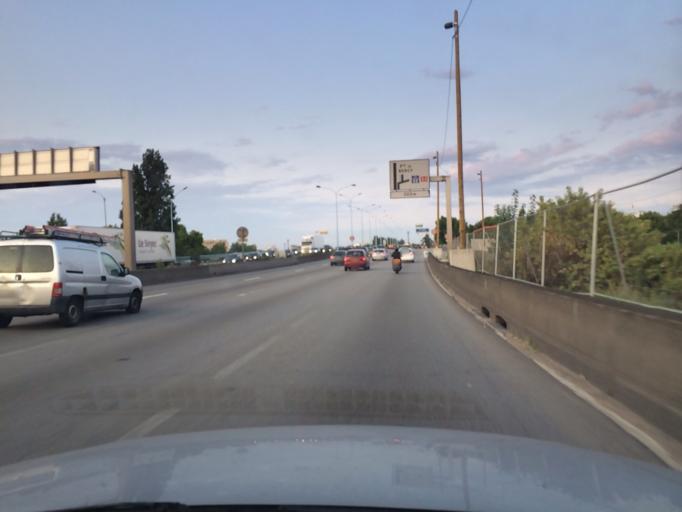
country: FR
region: Ile-de-France
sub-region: Departement du Val-de-Marne
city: Ivry-sur-Seine
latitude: 48.8251
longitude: 2.3860
